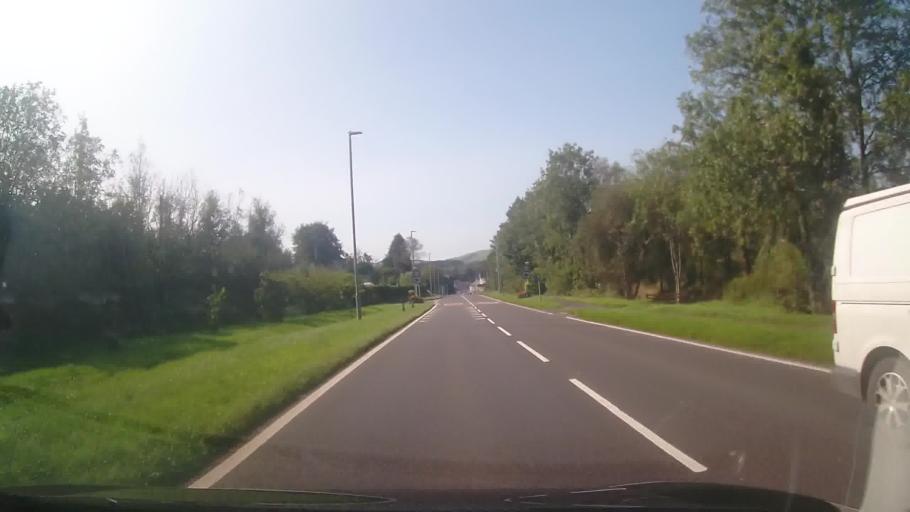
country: GB
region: Wales
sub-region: Carmarthenshire
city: Llandovery
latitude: 52.1096
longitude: -3.6345
